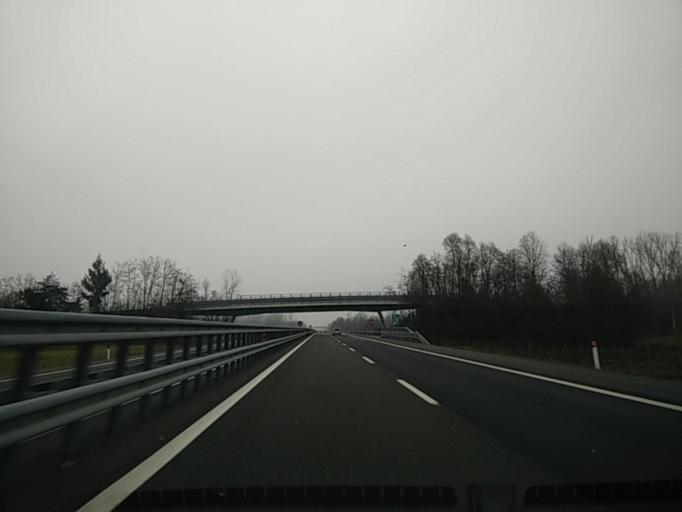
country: IT
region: Piedmont
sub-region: Provincia di Asti
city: Villafranca d'Asti
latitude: 44.9283
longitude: 8.0085
